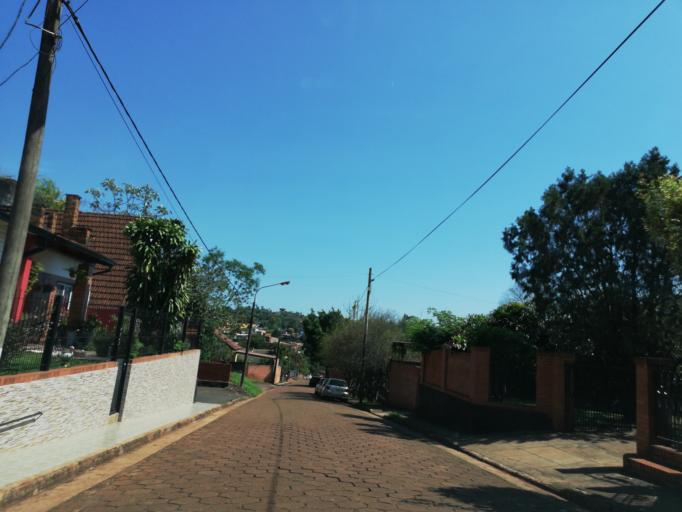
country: AR
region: Misiones
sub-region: Departamento de Eldorado
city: Eldorado
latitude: -26.4083
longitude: -54.6116
